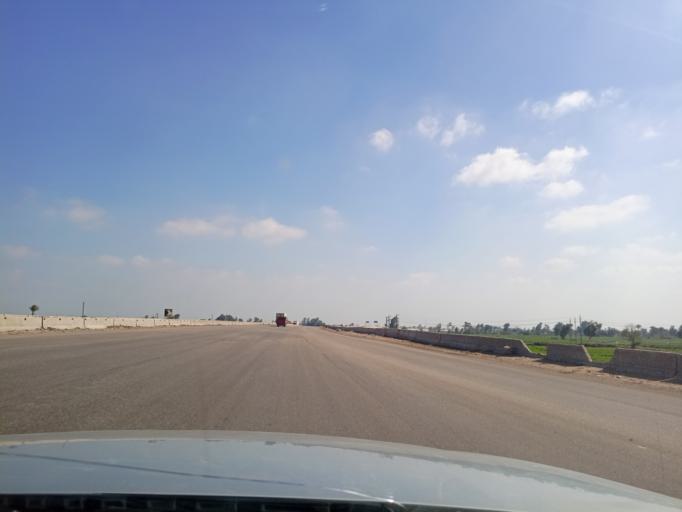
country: EG
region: Eastern Province
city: Mashtul as Suq
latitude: 30.4625
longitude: 31.3720
